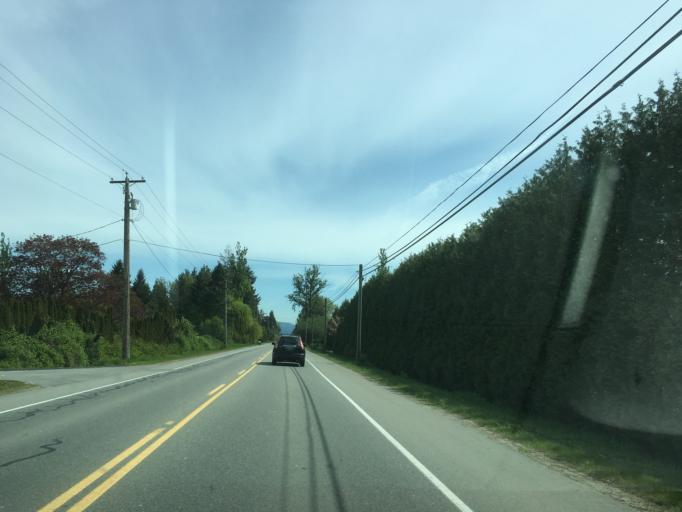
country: CA
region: British Columbia
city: Pitt Meadows
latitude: 49.2442
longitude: -122.7034
